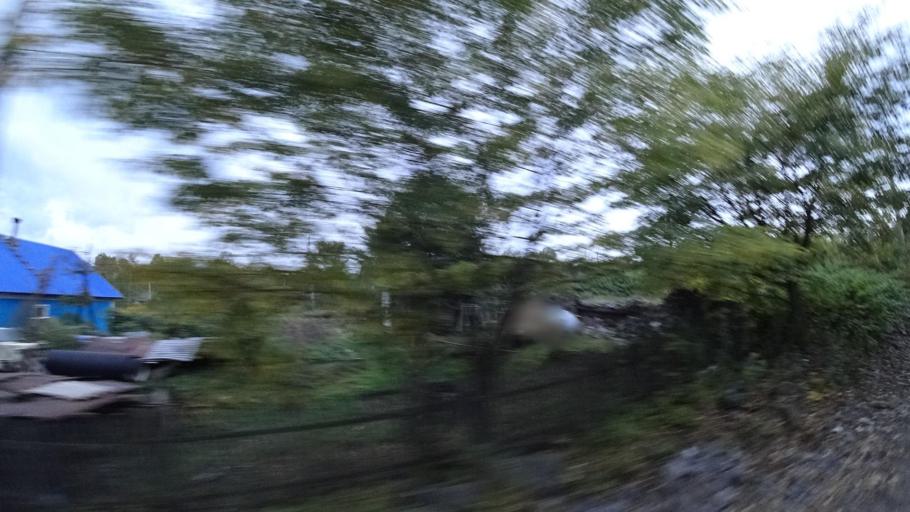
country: RU
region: Jewish Autonomous Oblast
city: Izvestkovyy
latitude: 48.9812
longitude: 131.5540
